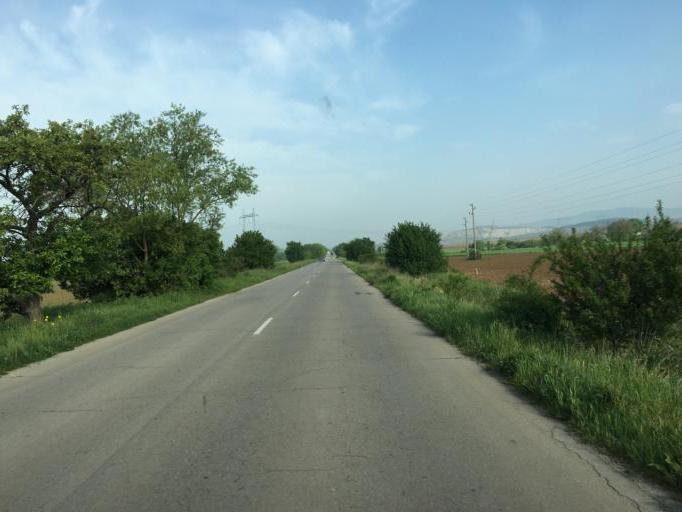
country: BG
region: Pernik
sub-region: Obshtina Radomir
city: Radomir
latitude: 42.4840
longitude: 23.0542
